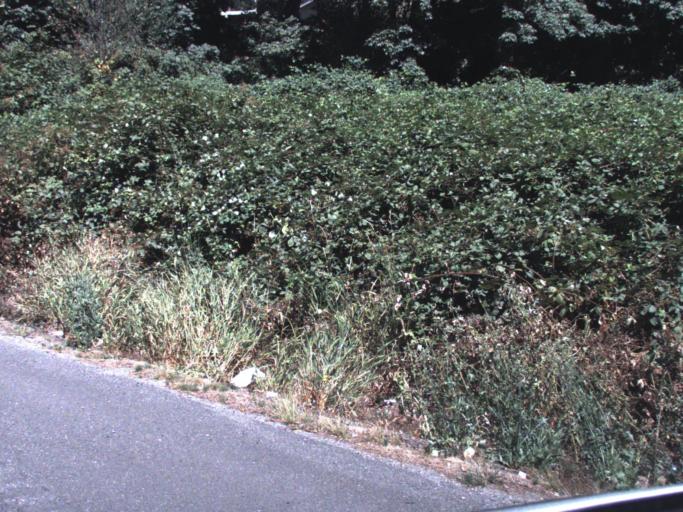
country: US
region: Washington
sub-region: King County
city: Tukwila
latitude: 47.4921
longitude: -122.2642
